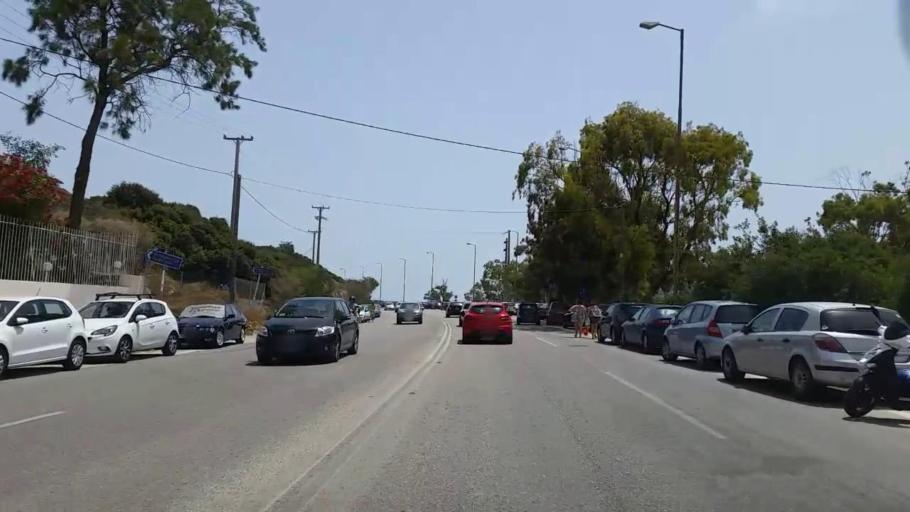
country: GR
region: Attica
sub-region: Nomarchia Anatolikis Attikis
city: Saronida
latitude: 37.7253
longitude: 23.9082
